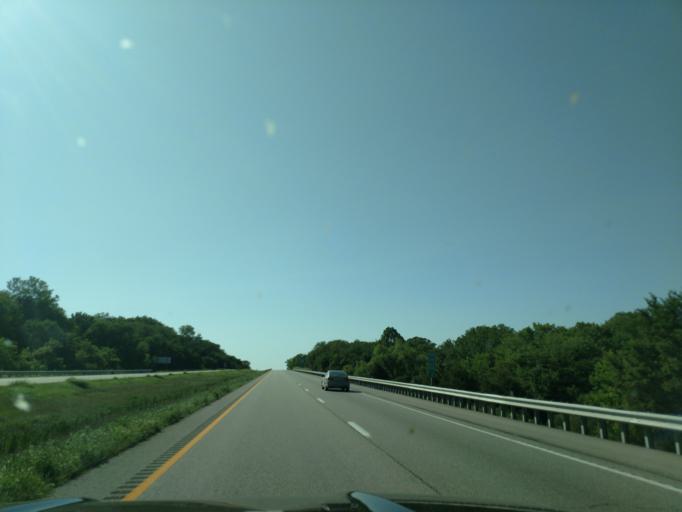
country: US
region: Missouri
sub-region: Andrew County
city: Savannah
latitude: 39.9055
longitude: -94.8875
